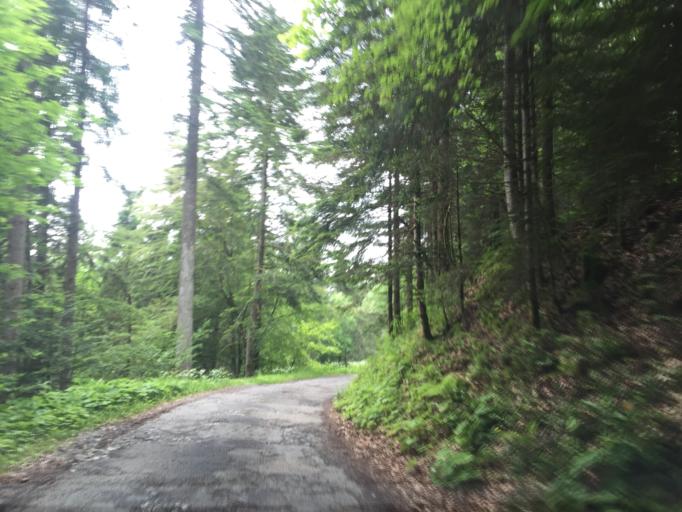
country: FR
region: Rhone-Alpes
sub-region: Departement de la Savoie
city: La Rochette
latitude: 45.4341
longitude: 6.1701
